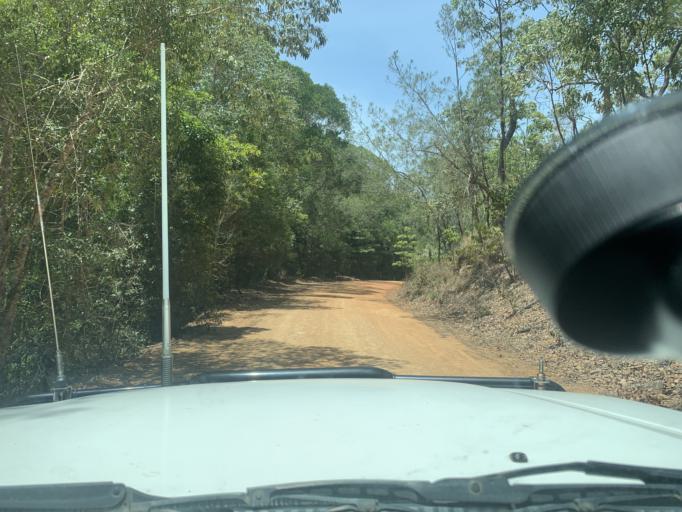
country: AU
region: Queensland
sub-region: Cairns
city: Redlynch
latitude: -16.9222
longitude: 145.6021
